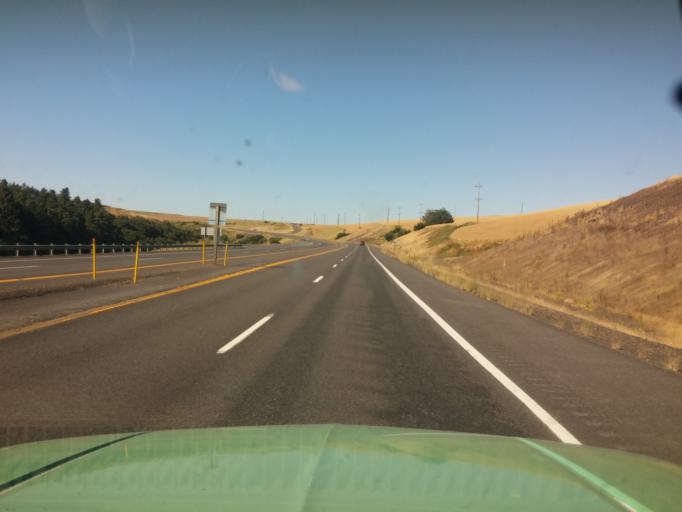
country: US
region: Idaho
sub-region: Nez Perce County
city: Lewiston
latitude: 46.4871
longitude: -117.0315
